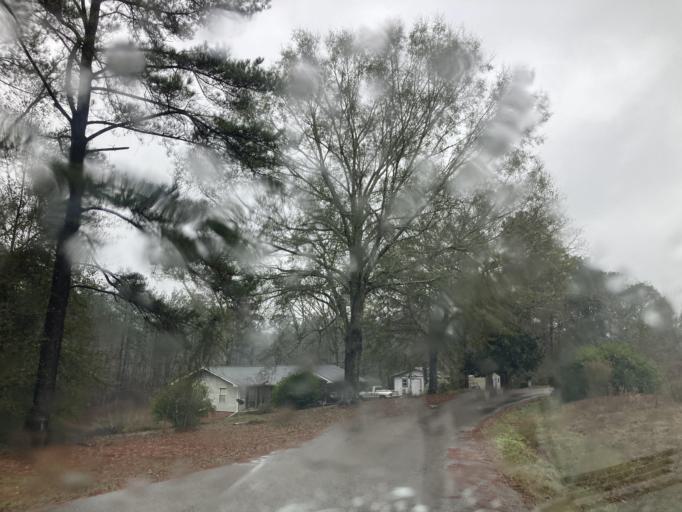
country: US
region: Mississippi
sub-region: Forrest County
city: Rawls Springs
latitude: 31.4951
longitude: -89.3617
